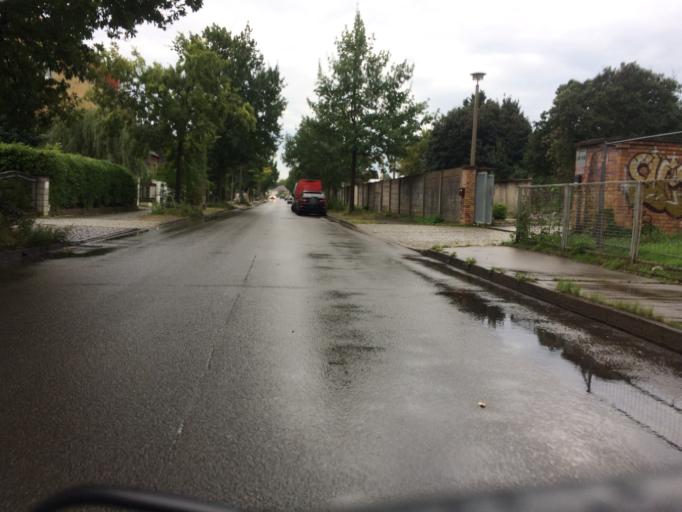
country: DE
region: Berlin
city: Buchholz
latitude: 52.5904
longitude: 13.4202
